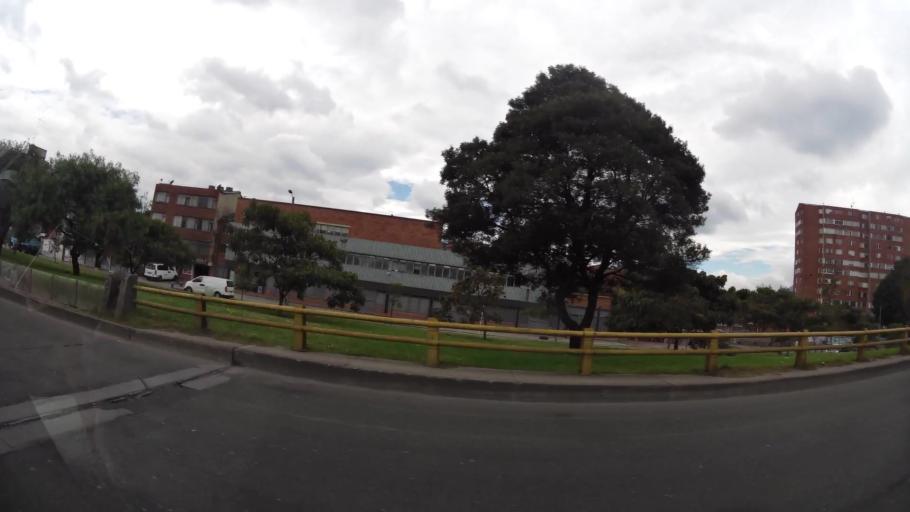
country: CO
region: Bogota D.C.
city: Bogota
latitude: 4.6252
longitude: -74.0848
